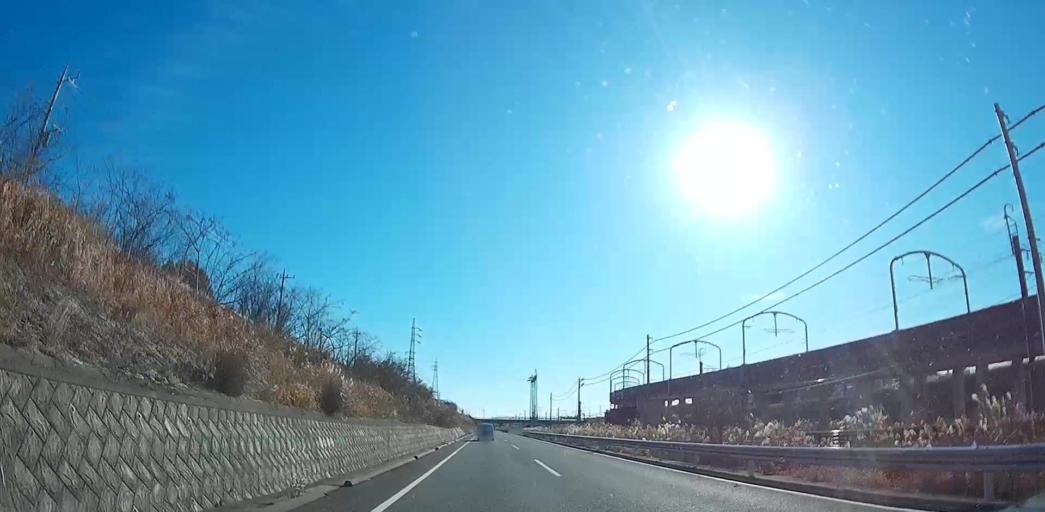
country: JP
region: Ibaraki
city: Ryugasaki
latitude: 35.8003
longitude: 140.1762
